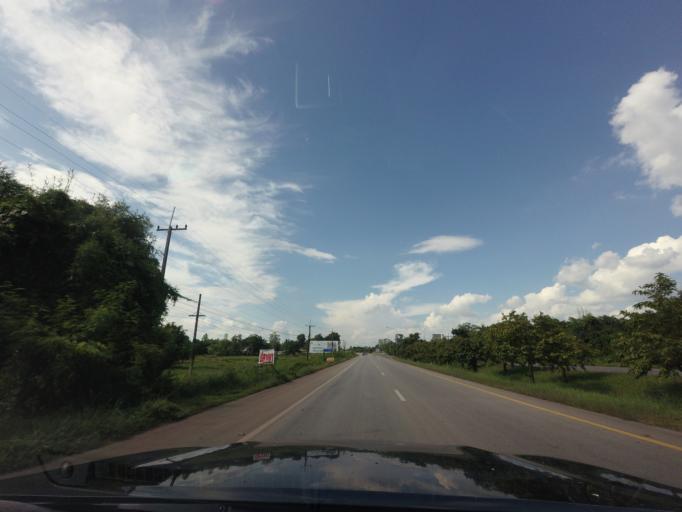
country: TH
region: Nong Khai
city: Sa Khrai
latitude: 17.6684
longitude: 102.7906
